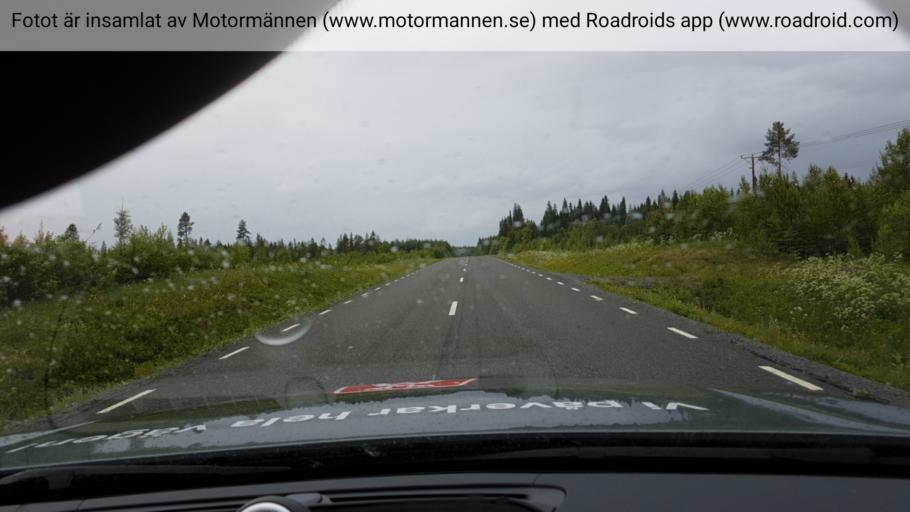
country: SE
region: Jaemtland
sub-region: Stroemsunds Kommun
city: Stroemsund
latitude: 63.6485
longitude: 15.1684
